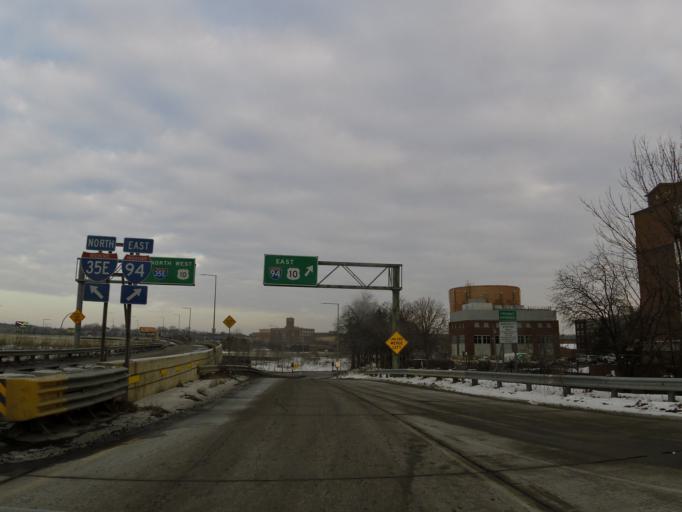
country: US
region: Minnesota
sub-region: Ramsey County
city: Saint Paul
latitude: 44.9529
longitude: -93.0939
